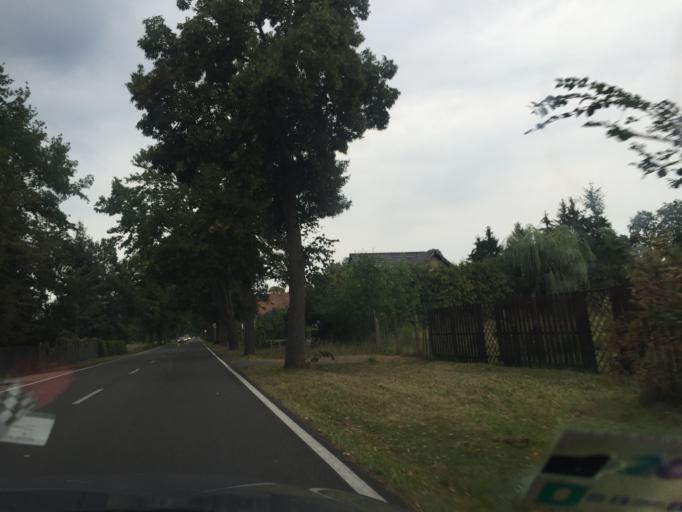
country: DE
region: Brandenburg
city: Wandlitz
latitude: 52.7553
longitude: 13.3880
